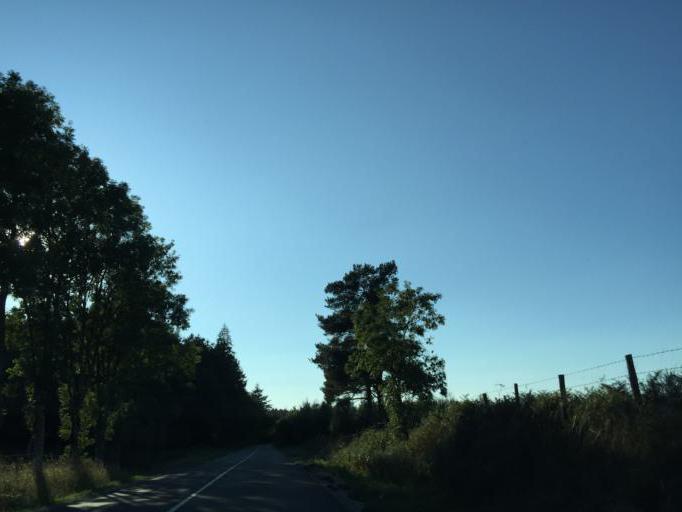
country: FR
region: Midi-Pyrenees
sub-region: Departement de l'Aveyron
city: Salles-Curan
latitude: 44.1610
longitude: 2.8488
